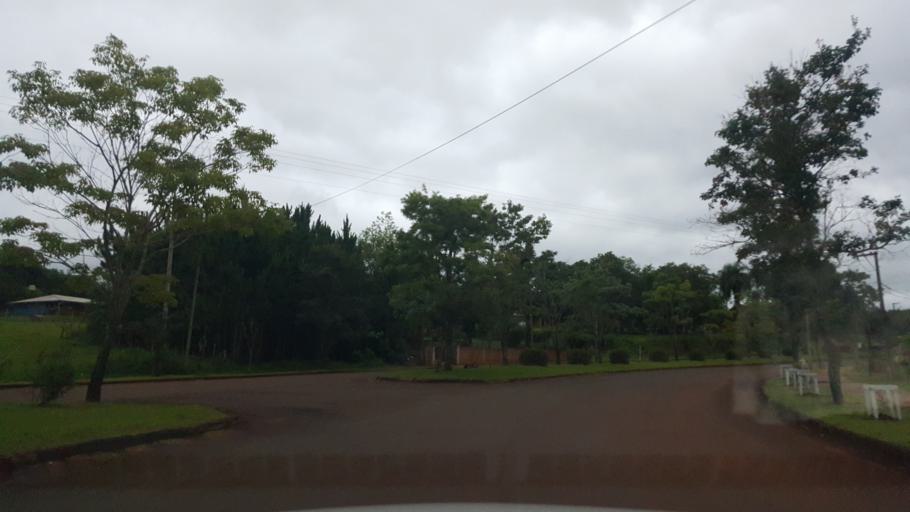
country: AR
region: Misiones
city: Ruiz de Montoya
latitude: -26.9827
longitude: -55.0511
